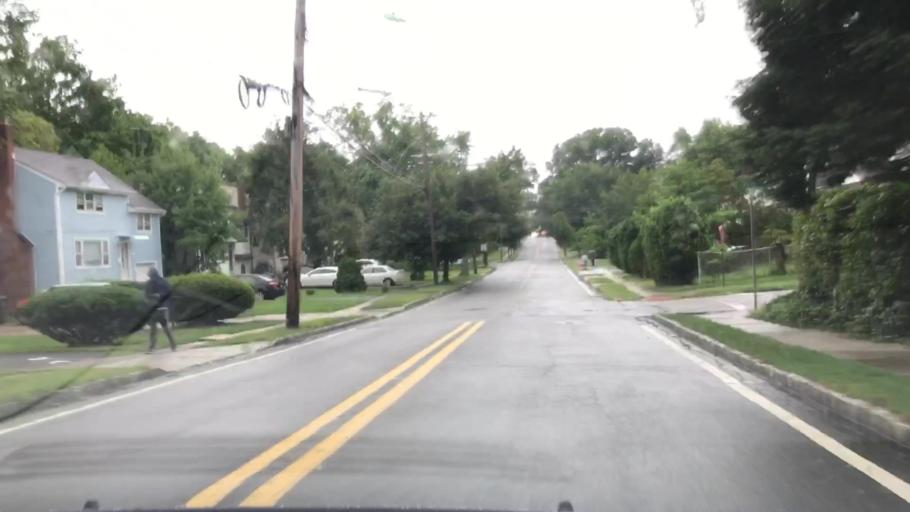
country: US
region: New Jersey
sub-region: Bergen County
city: Englewood
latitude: 40.9024
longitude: -73.9839
